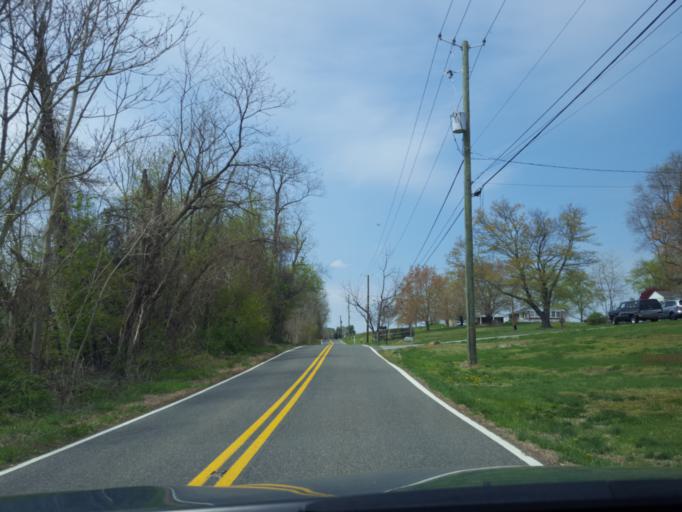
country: US
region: Maryland
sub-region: Prince George's County
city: Croom
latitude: 38.7419
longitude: -76.7366
